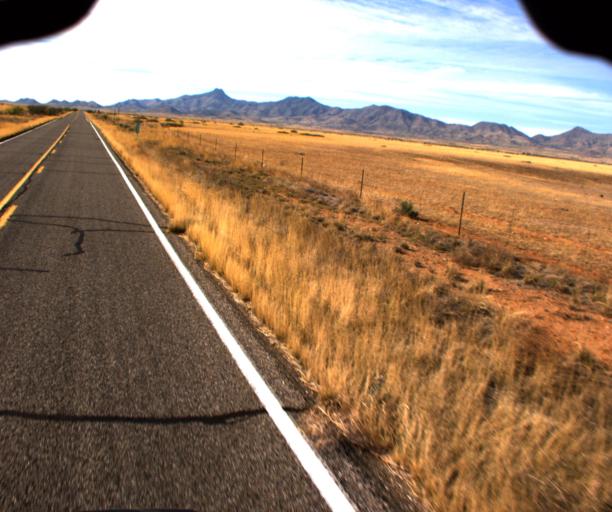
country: US
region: Arizona
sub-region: Cochise County
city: Willcox
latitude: 32.0802
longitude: -109.5210
